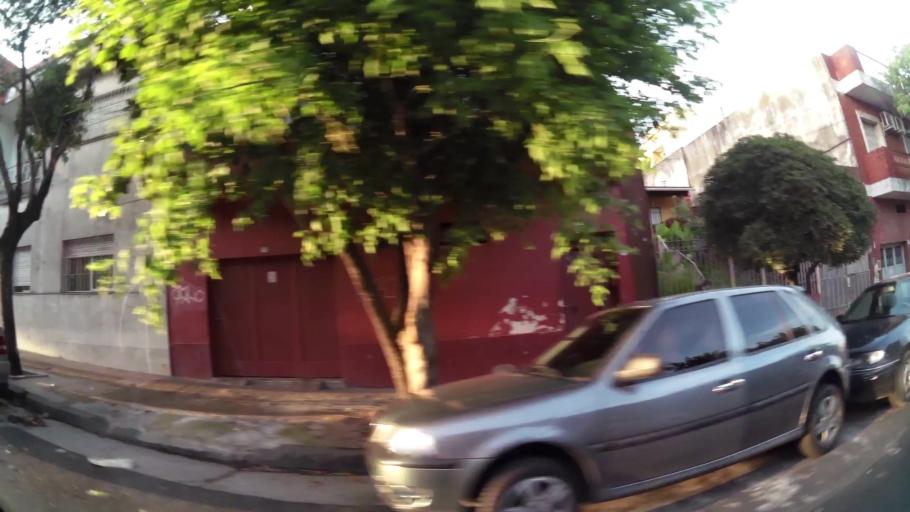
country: AR
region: Buenos Aires F.D.
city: Buenos Aires
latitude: -34.6394
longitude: -58.4258
